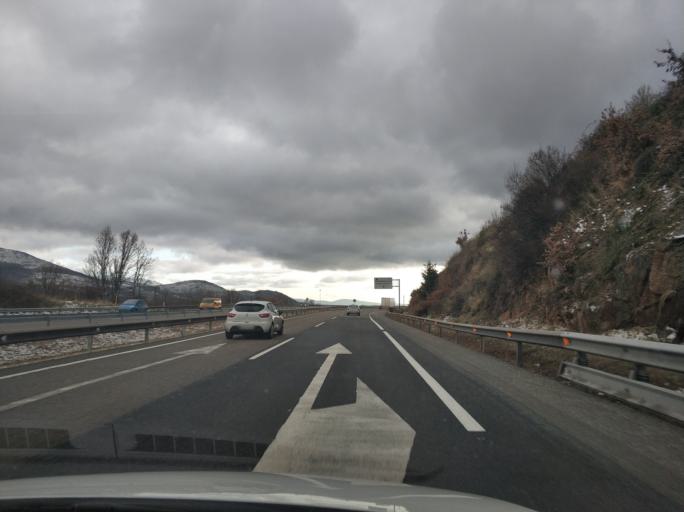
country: ES
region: Madrid
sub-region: Provincia de Madrid
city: Robregordo
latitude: 41.1015
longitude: -3.5926
